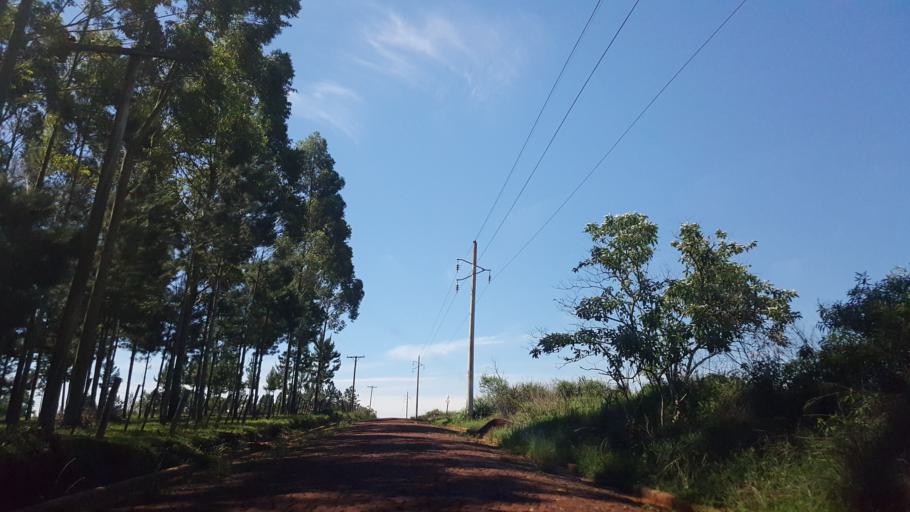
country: AR
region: Misiones
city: Capiovi
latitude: -26.9300
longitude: -55.0719
